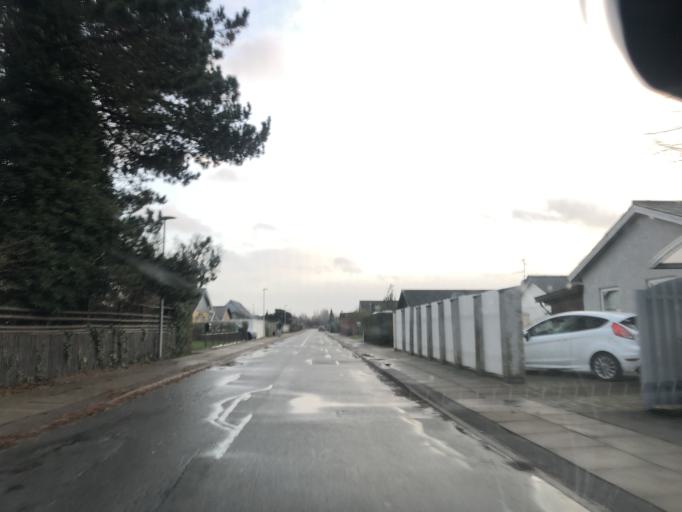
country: DK
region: Capital Region
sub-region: Tarnby Kommune
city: Tarnby
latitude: 55.6148
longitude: 12.6048
